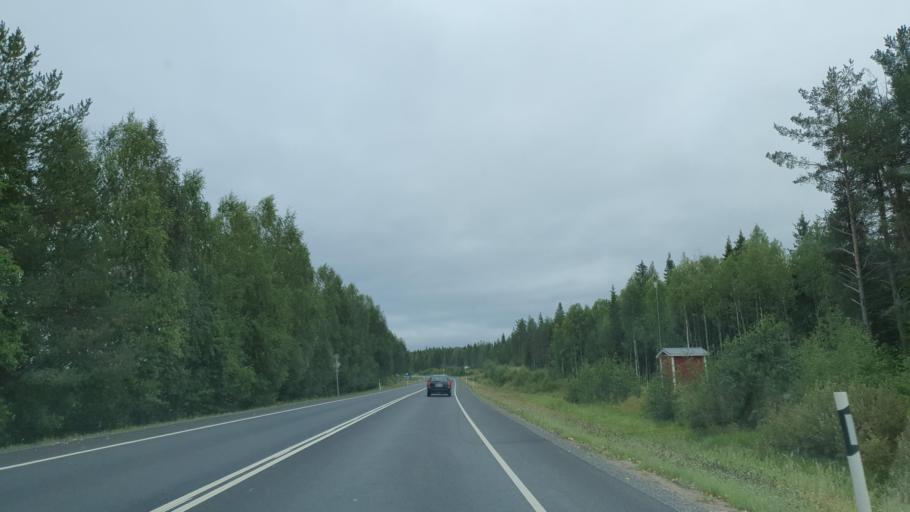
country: FI
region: Lapland
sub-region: Rovaniemi
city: Rovaniemi
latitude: 66.5991
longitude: 25.5933
